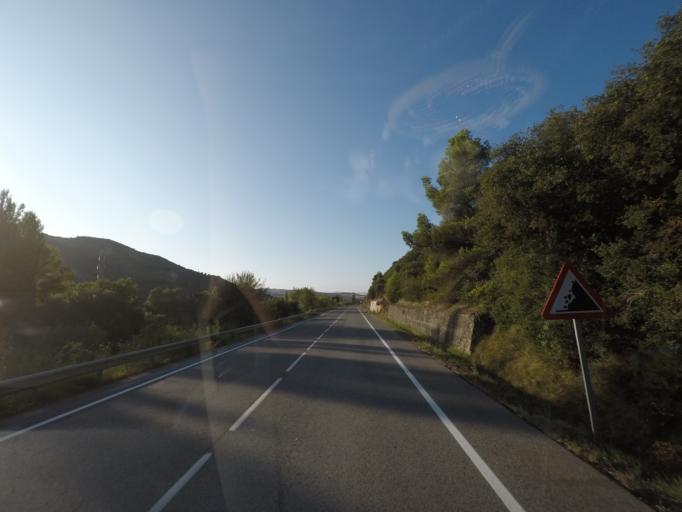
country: ES
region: Navarre
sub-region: Provincia de Navarra
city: Liedena
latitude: 42.6039
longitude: -1.2774
